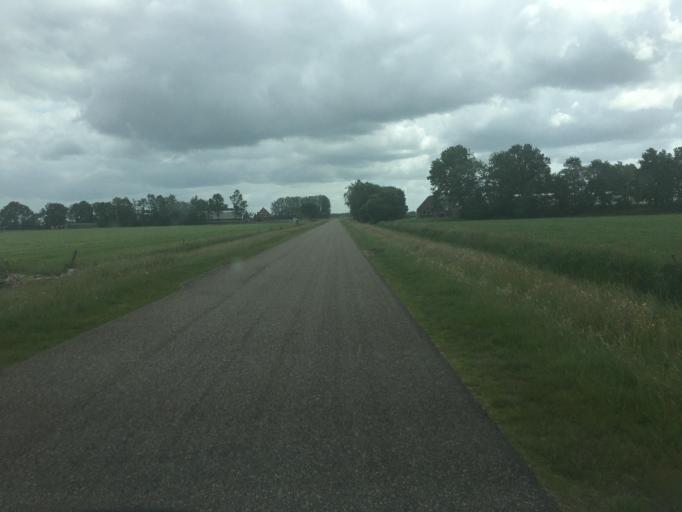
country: NL
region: Friesland
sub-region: Gemeente Heerenveen
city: Nieuwehorne
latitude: 52.9280
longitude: 6.0295
